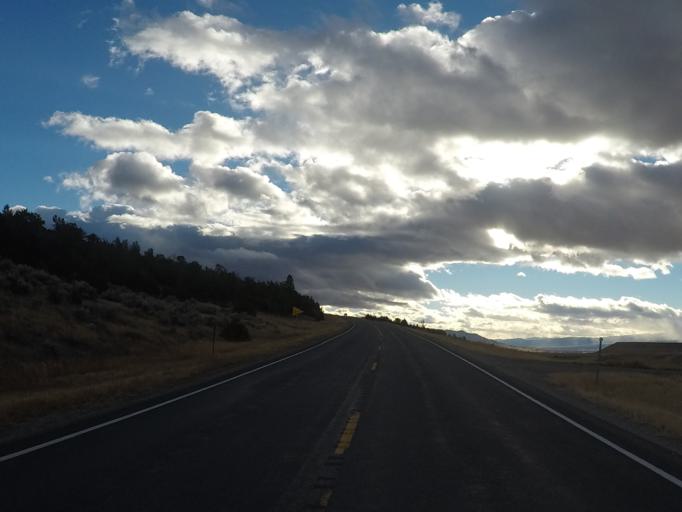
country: US
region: Montana
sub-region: Jefferson County
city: Whitehall
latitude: 45.8950
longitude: -111.9616
